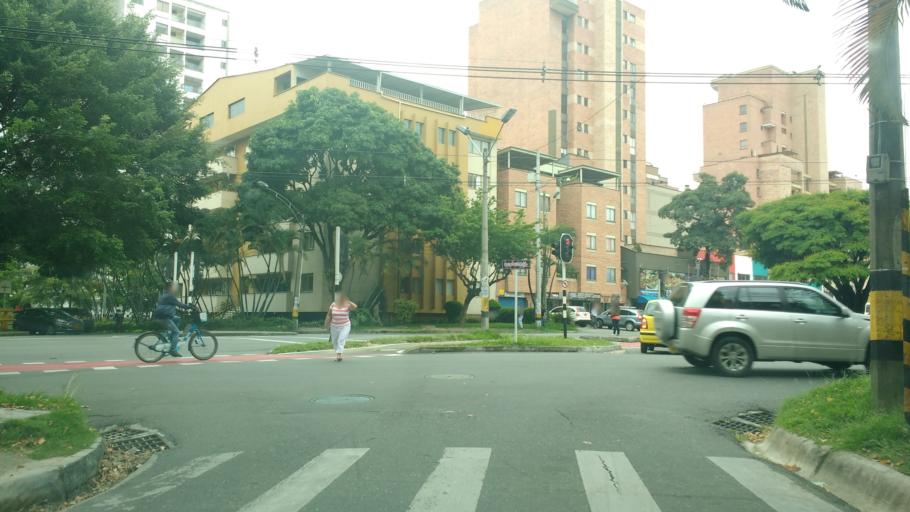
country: CO
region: Antioquia
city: Medellin
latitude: 6.2423
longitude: -75.5834
